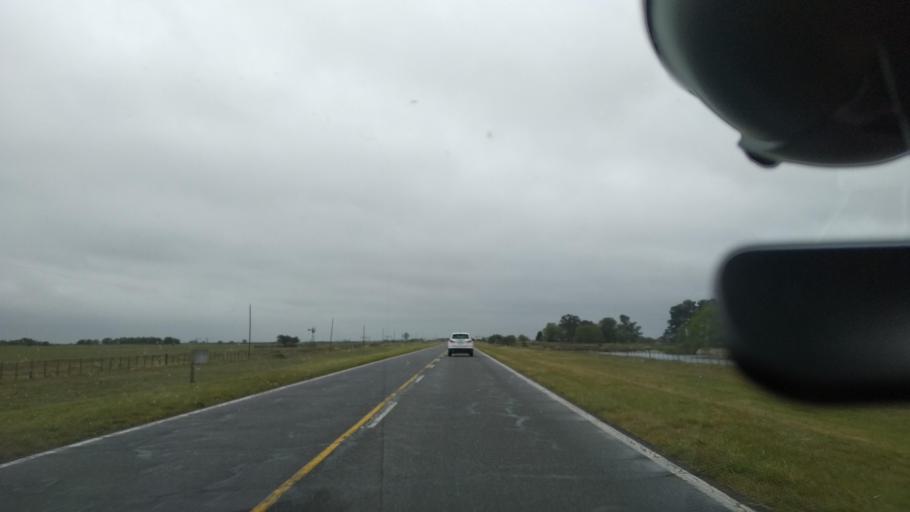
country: AR
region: Buenos Aires
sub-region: Partido de Dolores
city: Dolores
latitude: -36.1026
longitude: -57.4331
